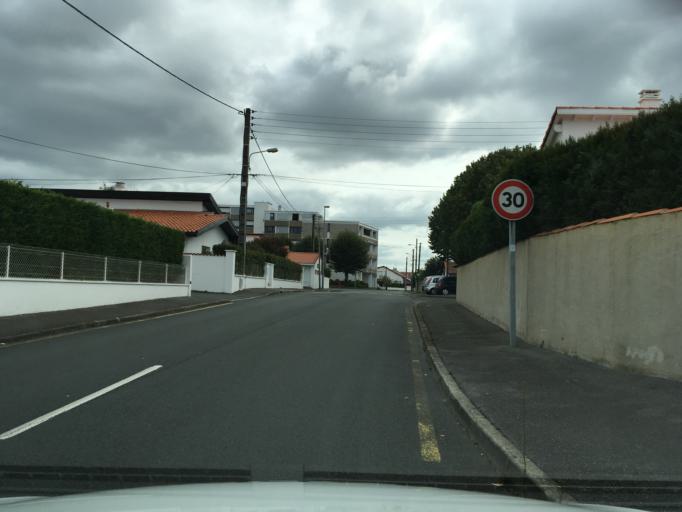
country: FR
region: Aquitaine
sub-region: Departement des Pyrenees-Atlantiques
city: Anglet
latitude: 43.4922
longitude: -1.5111
